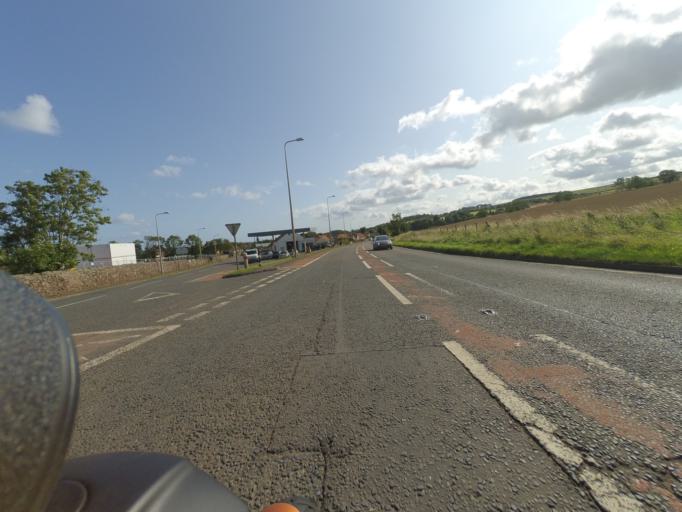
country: GB
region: Scotland
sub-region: East Lothian
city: East Linton
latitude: 55.9836
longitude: -2.6636
